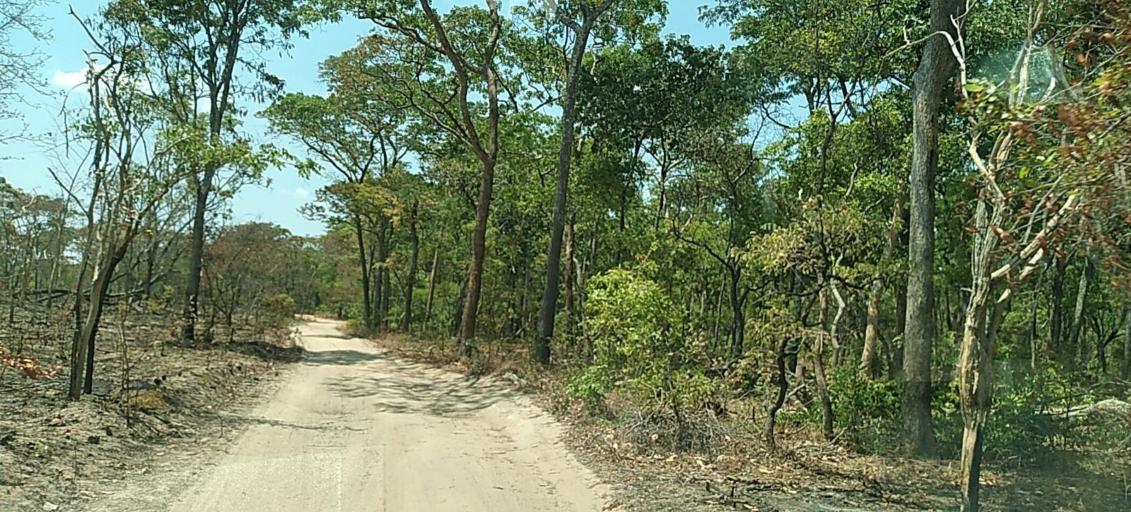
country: ZM
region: Copperbelt
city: Mpongwe
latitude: -13.6428
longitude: 28.4842
